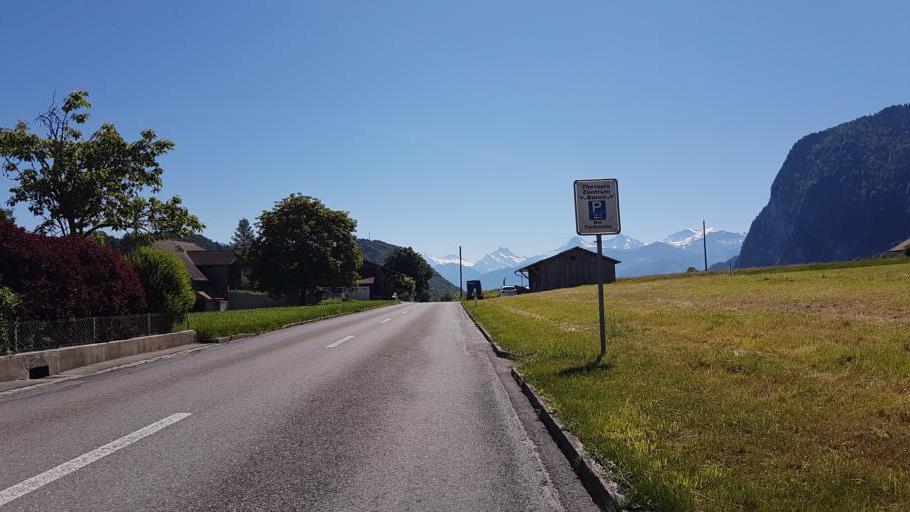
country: CH
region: Bern
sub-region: Thun District
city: Thierachern
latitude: 46.7144
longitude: 7.5634
